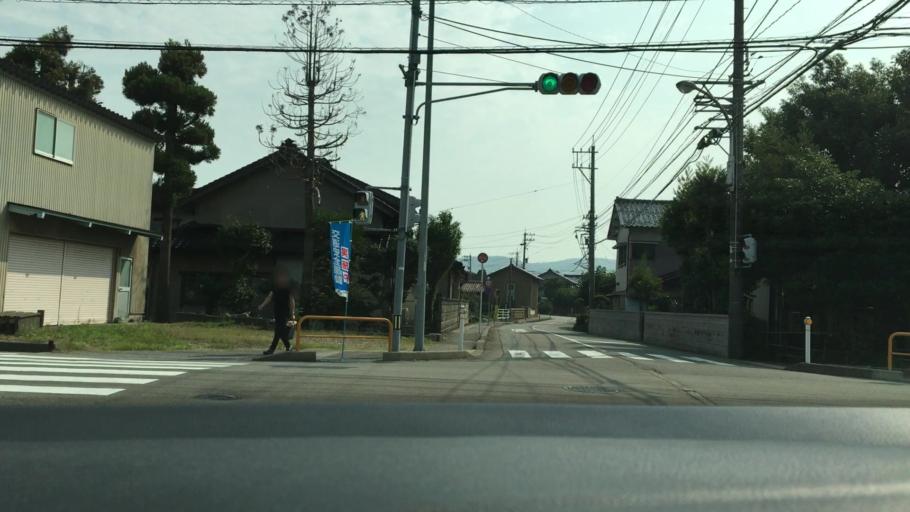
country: JP
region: Ishikawa
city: Nonoichi
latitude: 36.5079
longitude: 136.5992
